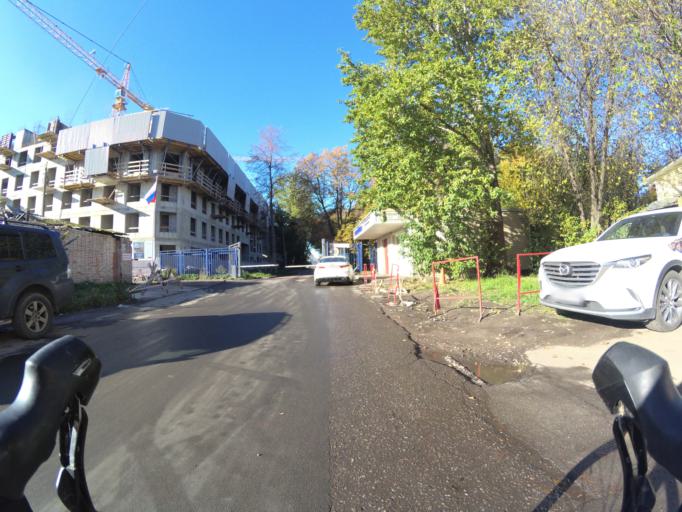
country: RU
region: Leningrad
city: Krestovskiy ostrov
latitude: 59.9630
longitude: 30.2474
